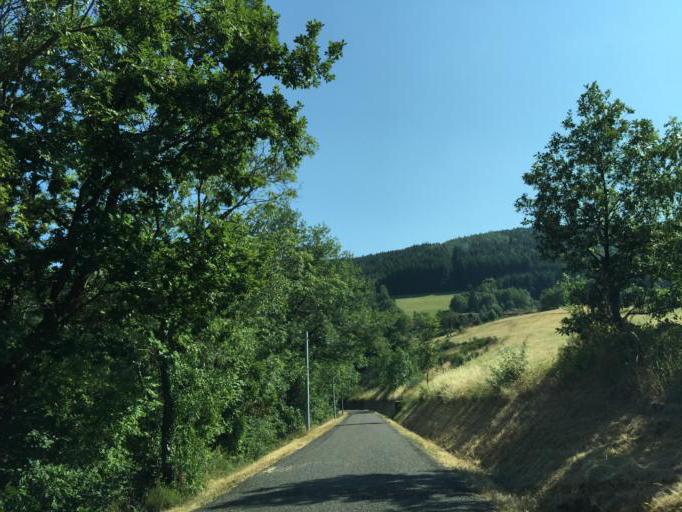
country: FR
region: Rhone-Alpes
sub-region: Departement de la Loire
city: Saint-Jean-Bonnefonds
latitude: 45.4328
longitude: 4.4791
